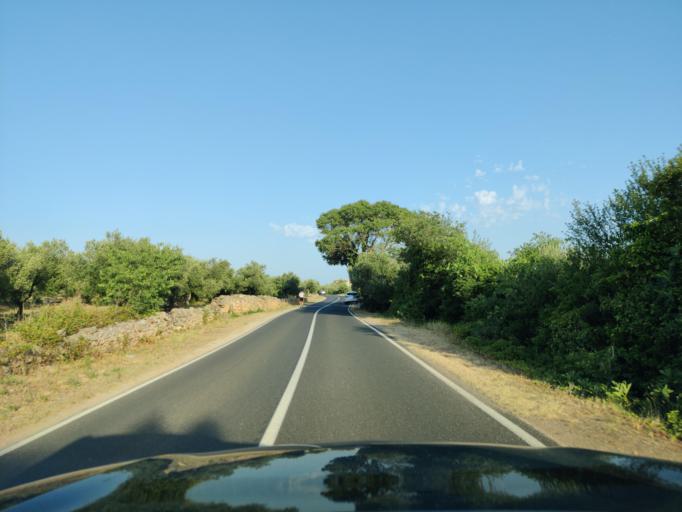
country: HR
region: Sibensko-Kniniska
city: Tribunj
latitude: 43.7691
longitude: 15.7289
